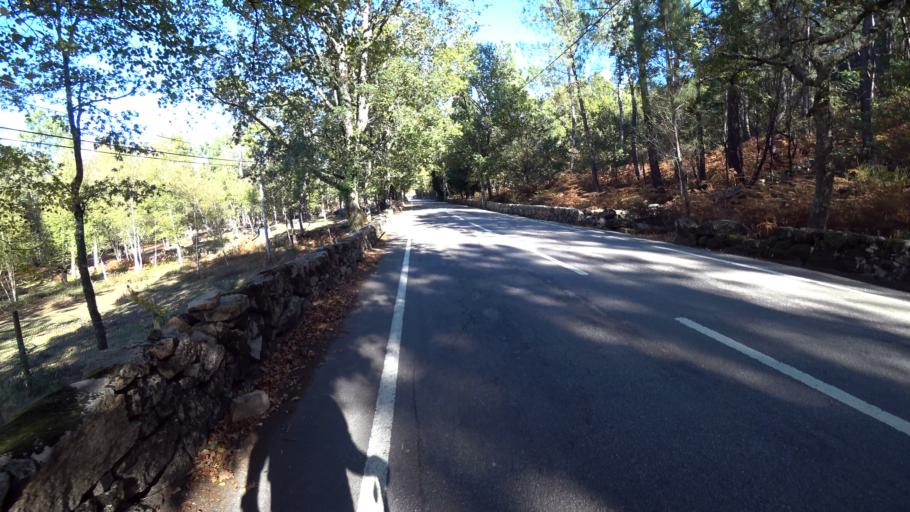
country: PT
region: Braga
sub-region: Vieira do Minho
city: Real
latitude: 41.7511
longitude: -8.1955
